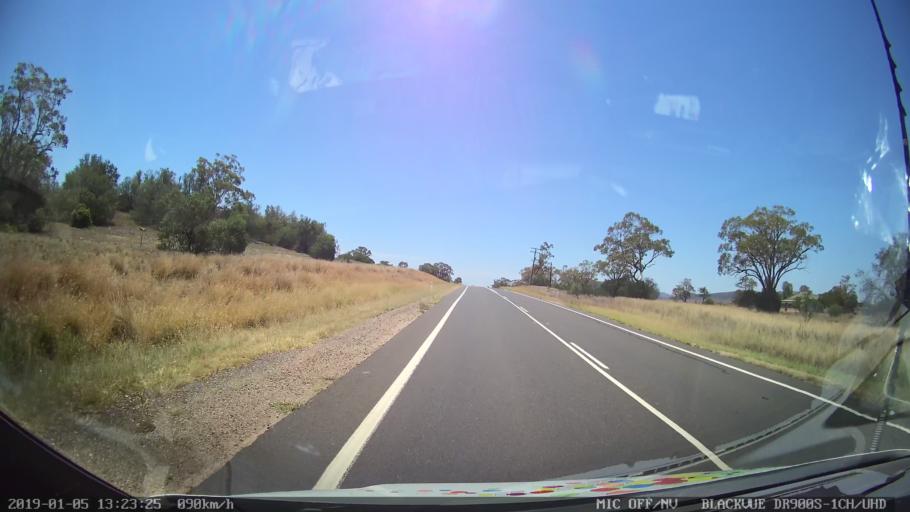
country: AU
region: New South Wales
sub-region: Gunnedah
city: Gunnedah
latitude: -31.0782
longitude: 149.9749
